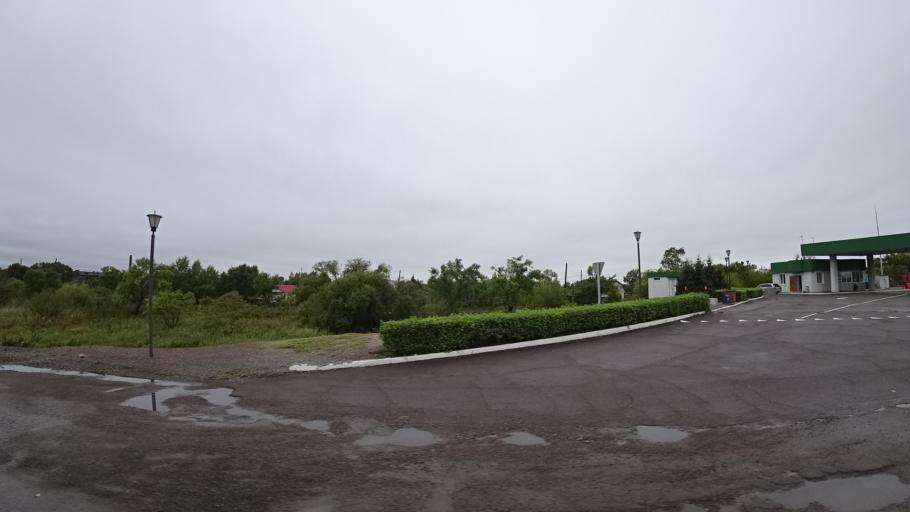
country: RU
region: Primorskiy
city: Monastyrishche
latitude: 44.2145
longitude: 132.4499
